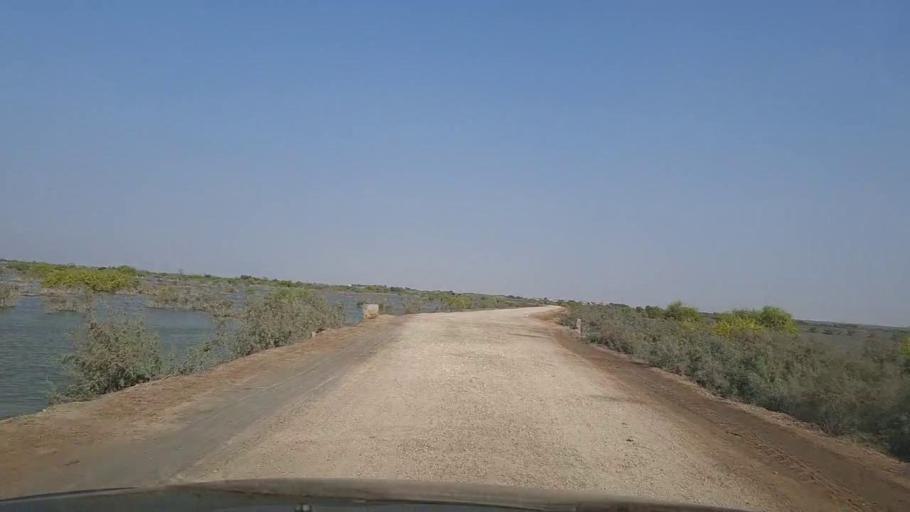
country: PK
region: Sindh
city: Thatta
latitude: 24.6409
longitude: 67.8145
